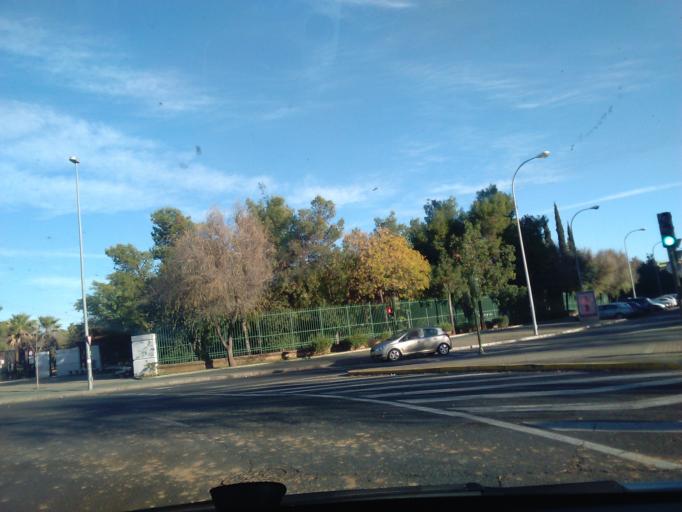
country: ES
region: Andalusia
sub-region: Provincia de Sevilla
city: Sevilla
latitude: 37.3800
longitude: -5.9541
